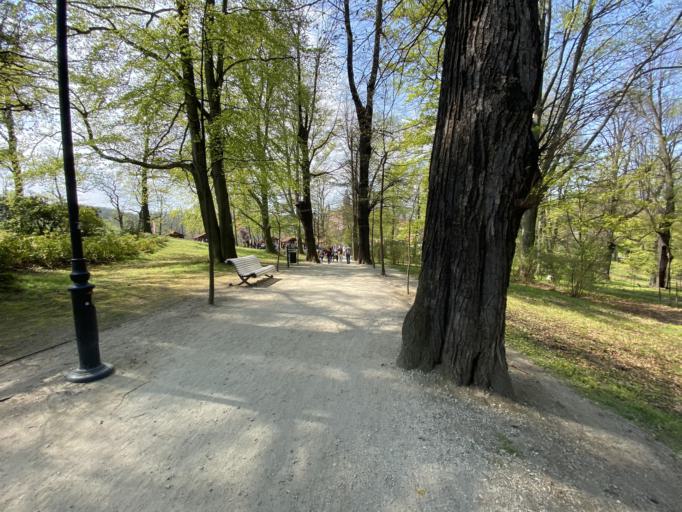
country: PL
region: Lower Silesian Voivodeship
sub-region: Powiat swidnicki
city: Swiebodzice
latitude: 50.8424
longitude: 16.2969
